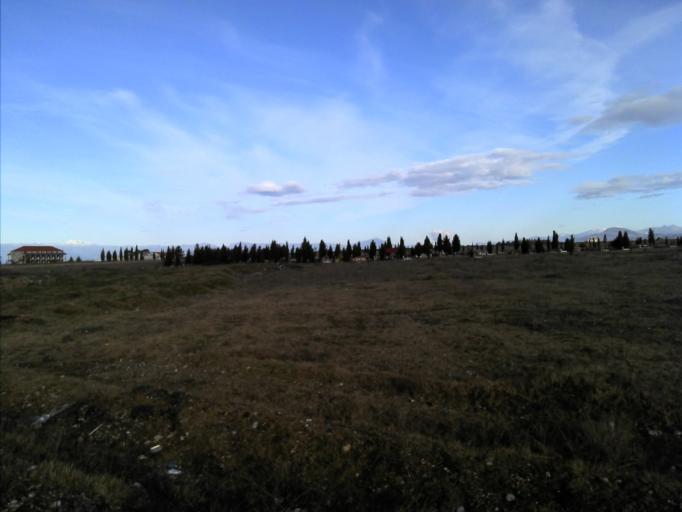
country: AL
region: Shkoder
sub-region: Rrethi i Malesia e Madhe
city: Koplik
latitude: 42.2219
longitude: 19.4334
